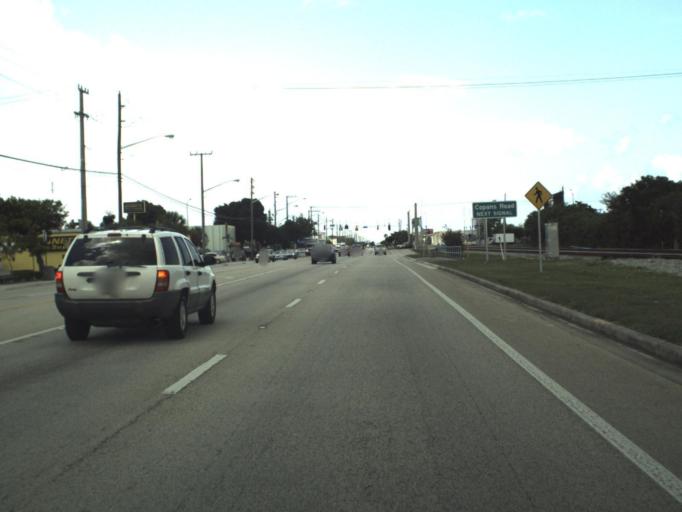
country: US
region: Florida
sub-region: Broward County
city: Kendall Green
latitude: 26.2583
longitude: -80.1185
